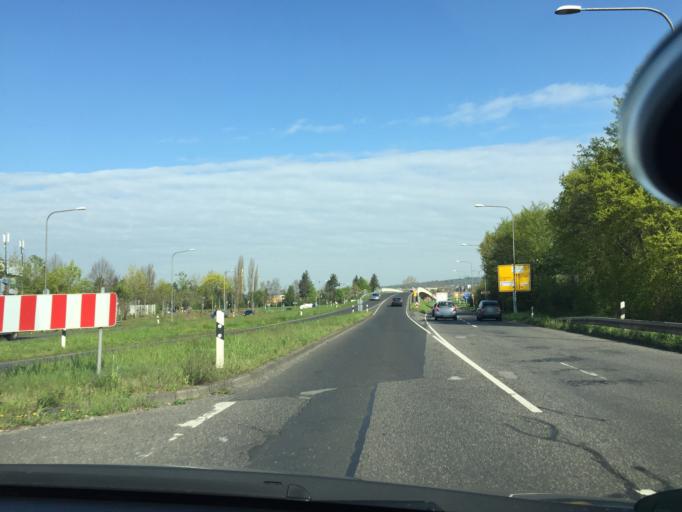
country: DE
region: Bavaria
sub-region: Regierungsbezirk Unterfranken
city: Aschaffenburg
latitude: 49.9703
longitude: 9.1326
